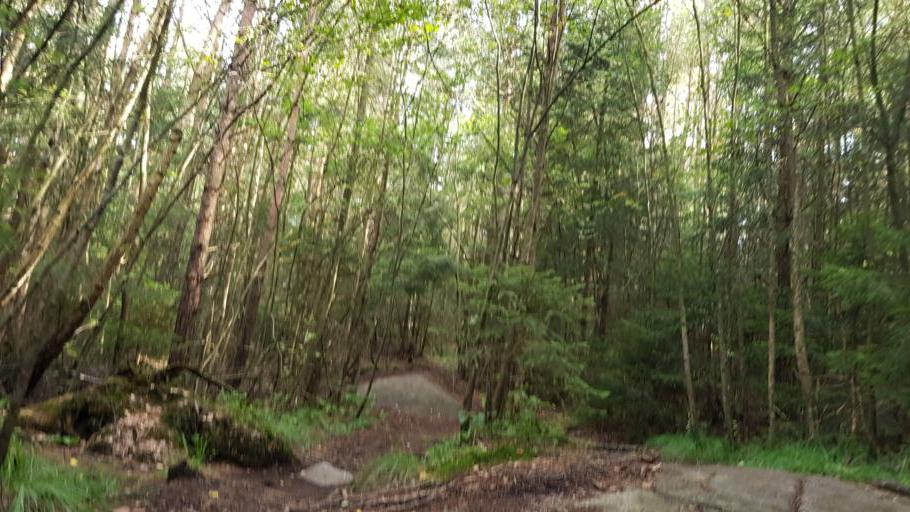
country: SE
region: Vaestra Goetaland
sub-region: Molndal
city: Moelndal
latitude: 57.6725
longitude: 12.0310
